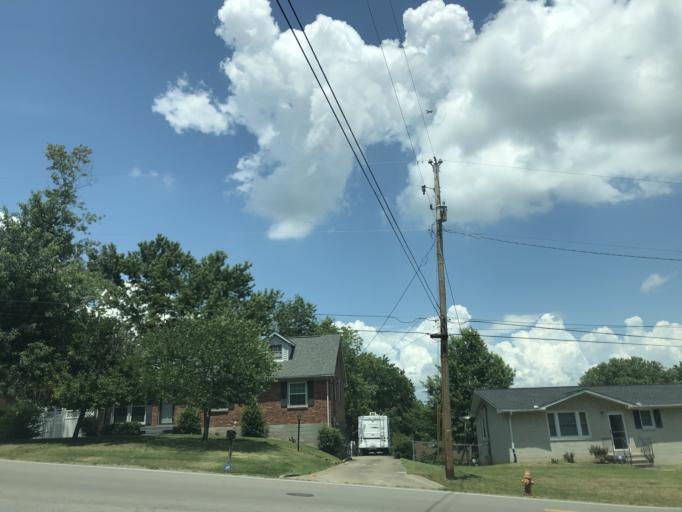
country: US
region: Tennessee
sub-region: Davidson County
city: Lakewood
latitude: 36.2001
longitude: -86.6254
